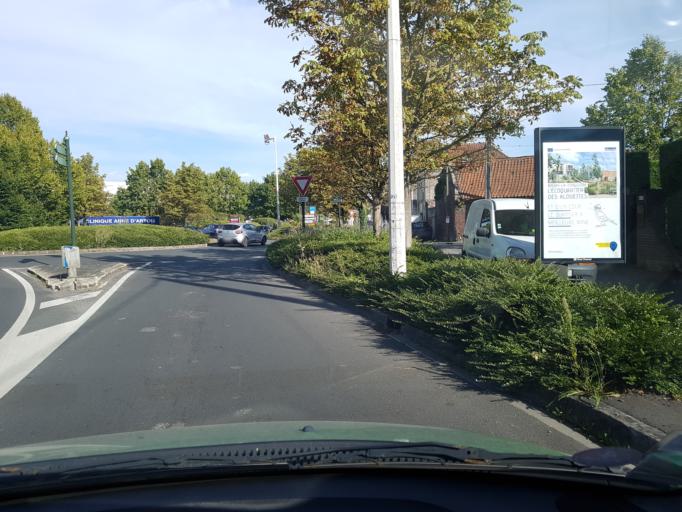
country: FR
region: Nord-Pas-de-Calais
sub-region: Departement du Pas-de-Calais
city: Bethune
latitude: 50.5393
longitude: 2.6275
